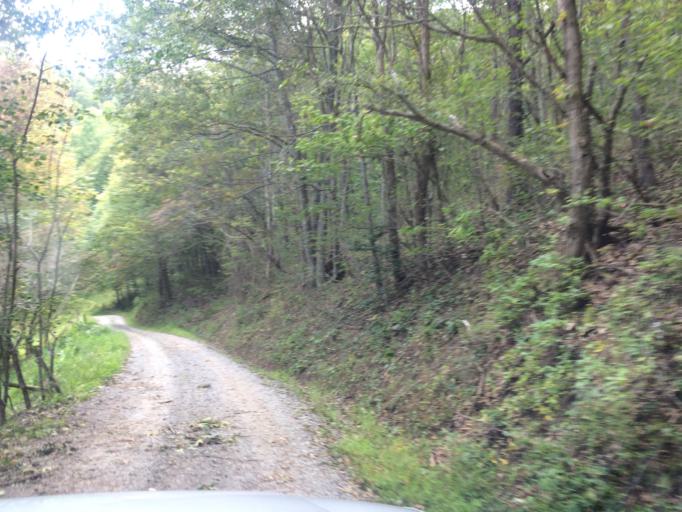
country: US
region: North Carolina
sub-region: Haywood County
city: Clyde
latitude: 35.5551
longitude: -82.9137
